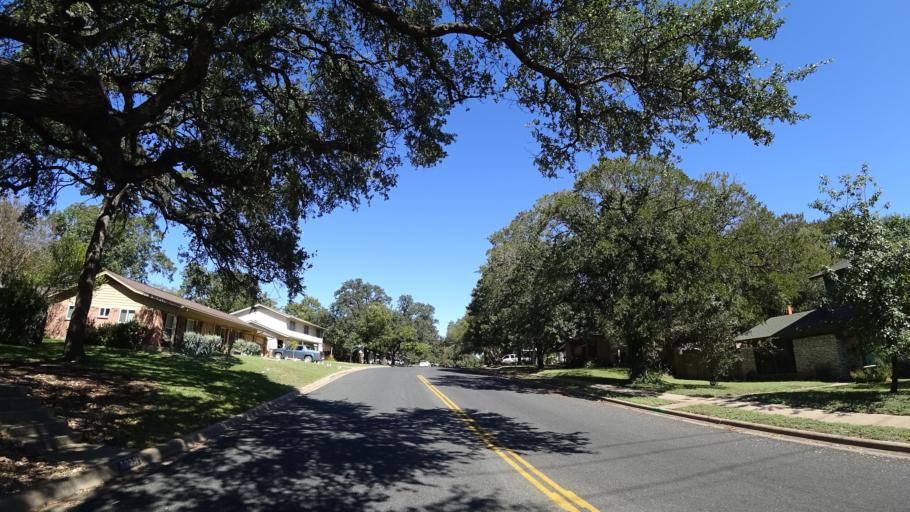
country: US
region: Texas
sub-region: Travis County
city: Rollingwood
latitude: 30.2245
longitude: -97.8013
